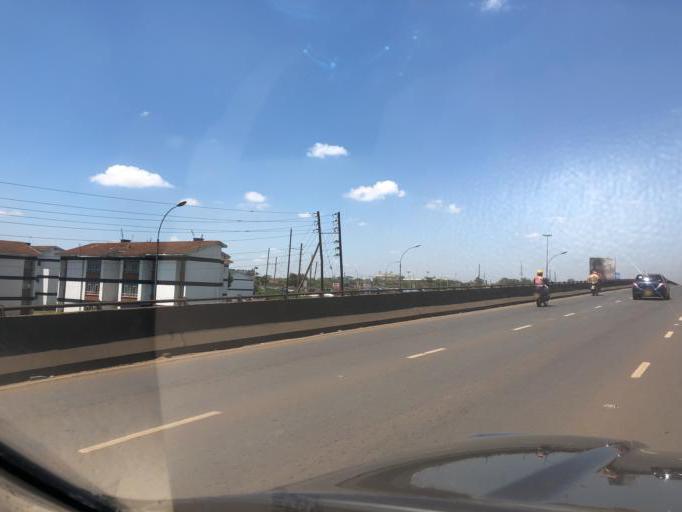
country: KE
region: Nairobi Area
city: Pumwani
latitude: -1.2185
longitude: 36.8928
